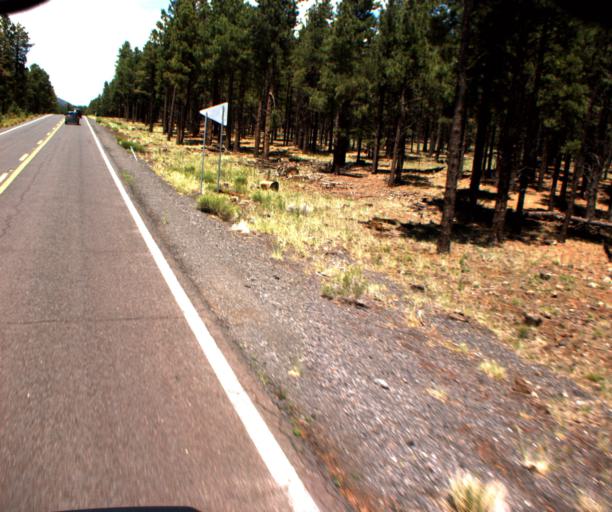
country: US
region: Arizona
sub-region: Coconino County
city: Parks
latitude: 35.4538
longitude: -111.7746
